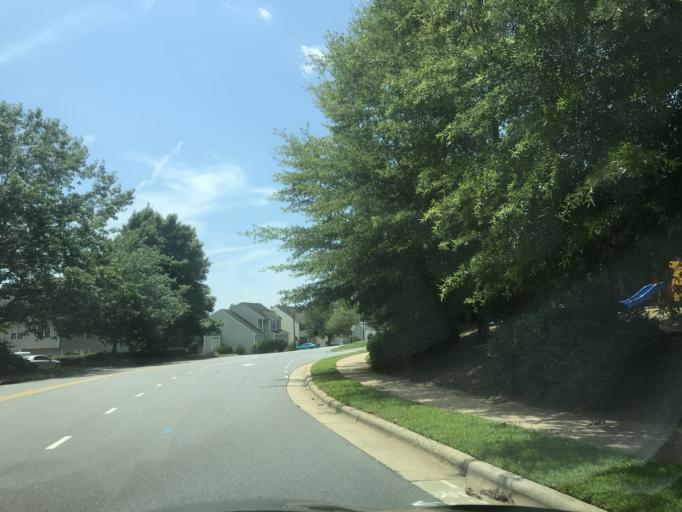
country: US
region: North Carolina
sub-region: Wake County
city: Wake Forest
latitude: 35.9393
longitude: -78.5610
